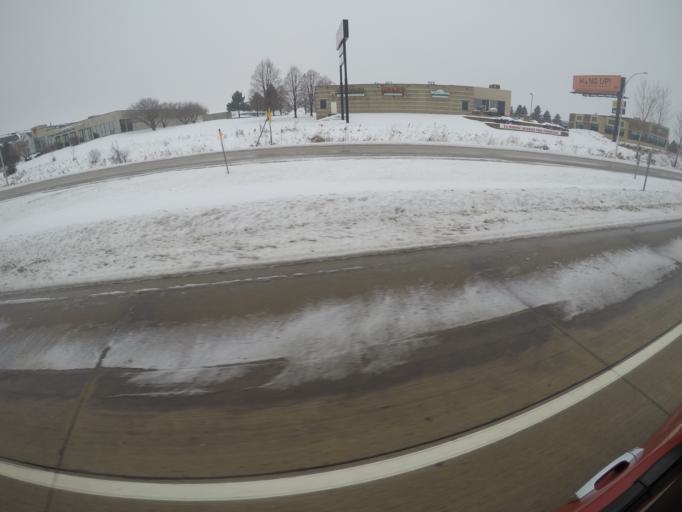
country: US
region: Minnesota
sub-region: Olmsted County
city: Rochester
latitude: 44.0686
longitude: -92.5021
